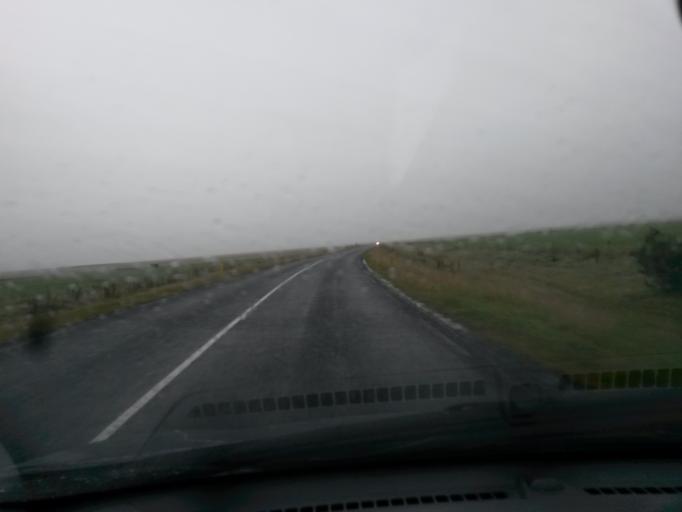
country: IS
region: South
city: Vestmannaeyjar
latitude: 63.5421
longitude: -19.6580
